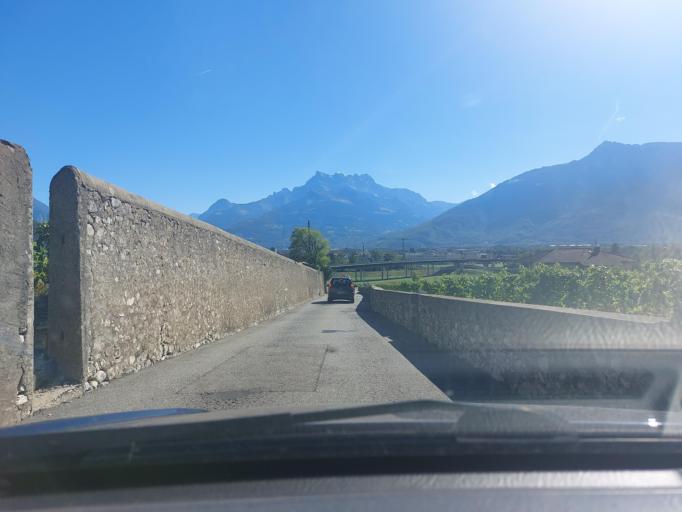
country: CH
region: Vaud
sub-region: Aigle District
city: Aigle
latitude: 46.3298
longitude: 6.9581
